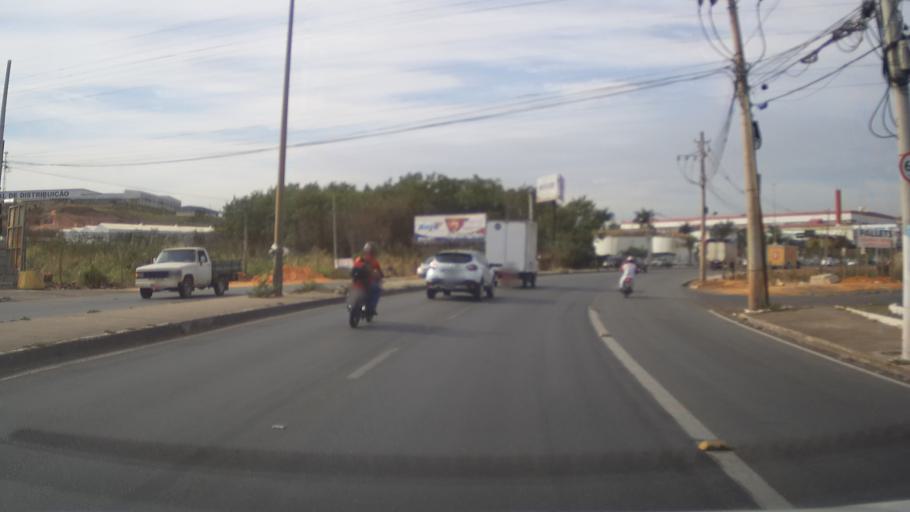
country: BR
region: Minas Gerais
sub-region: Contagem
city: Contagem
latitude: -19.9081
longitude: -44.0485
